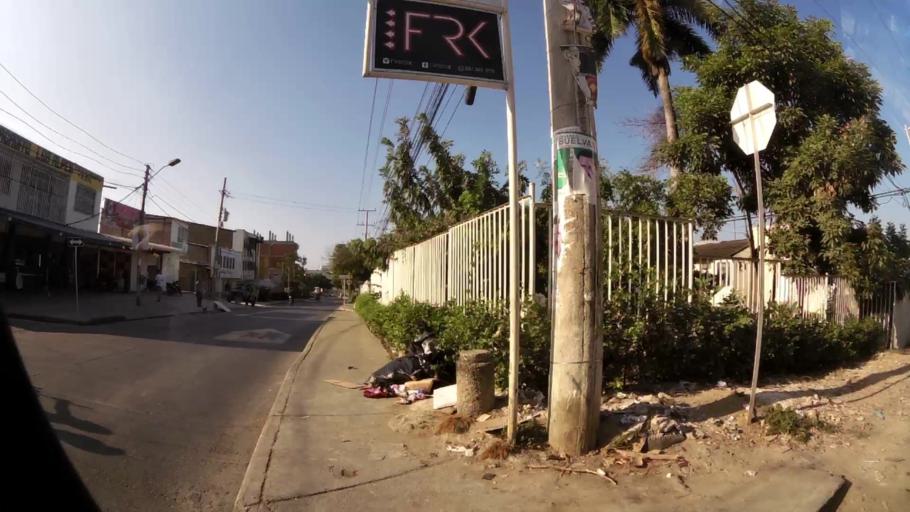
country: CO
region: Bolivar
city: Cartagena
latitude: 10.4005
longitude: -75.4812
